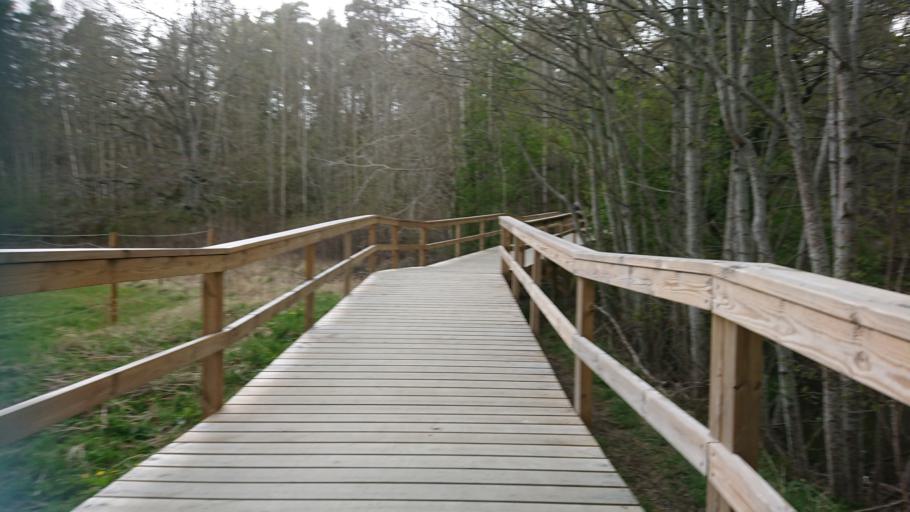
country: SE
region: Uppsala
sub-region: Uppsala Kommun
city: Uppsala
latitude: 59.7999
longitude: 17.6064
